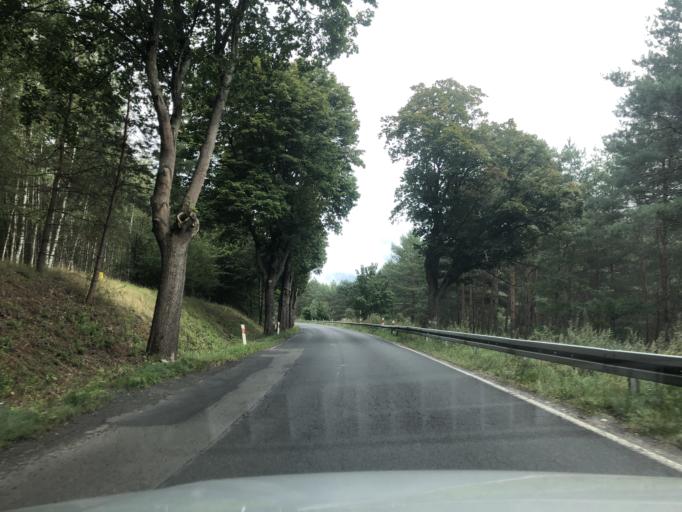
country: PL
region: Greater Poland Voivodeship
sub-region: Powiat czarnkowsko-trzcianecki
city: Krzyz Wielkopolski
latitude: 52.8626
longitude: 15.9639
